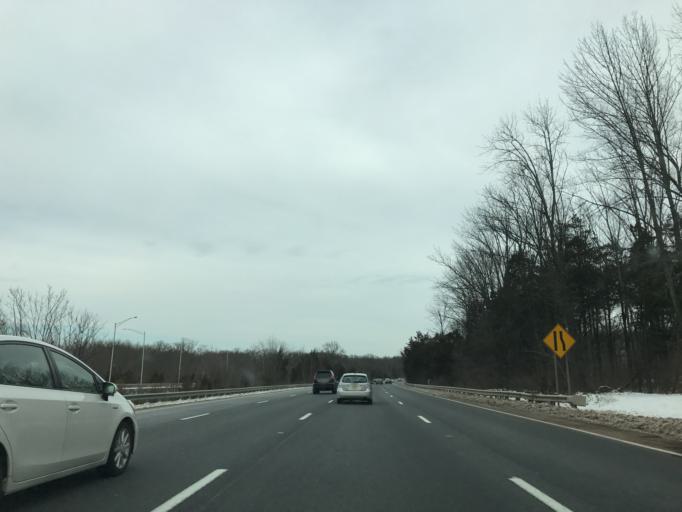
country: US
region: New Jersey
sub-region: Somerset County
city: Bedminster
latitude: 40.6594
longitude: -74.6435
